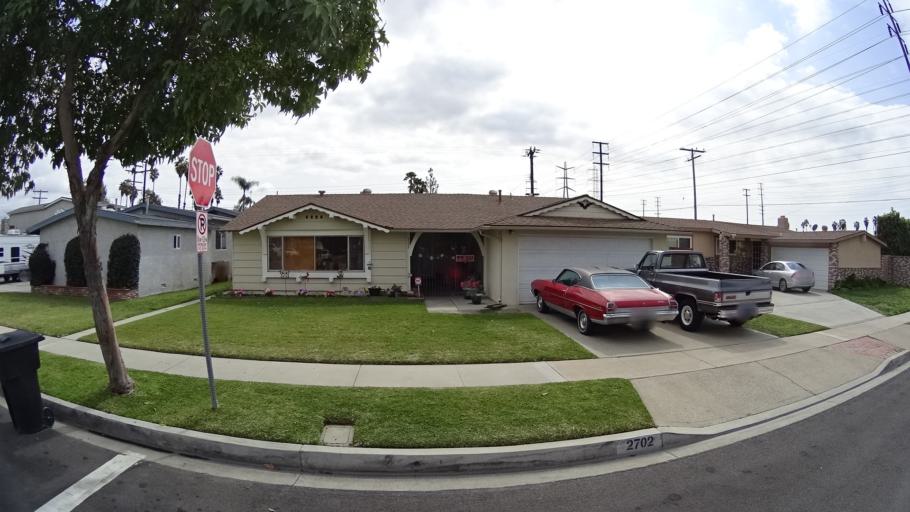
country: US
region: California
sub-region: Orange County
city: Stanton
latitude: 33.8342
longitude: -117.9801
